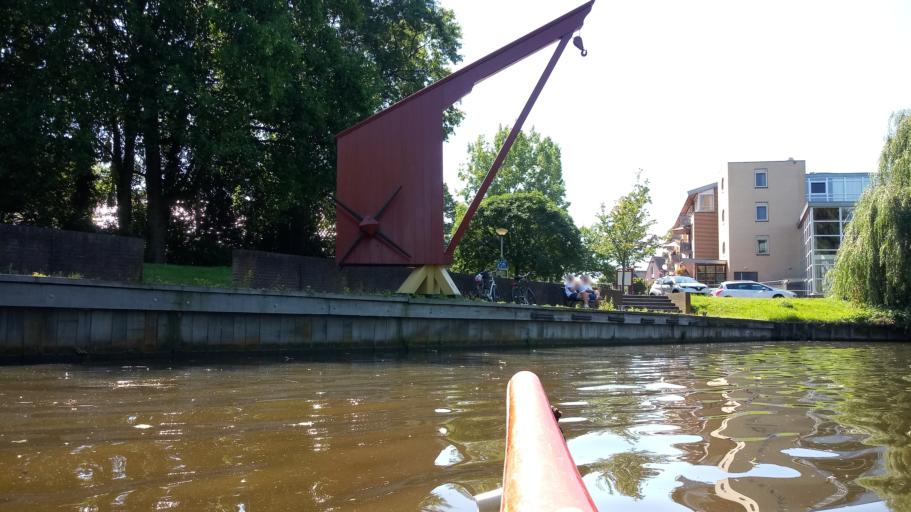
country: NL
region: Gelderland
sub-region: Berkelland
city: Eibergen
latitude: 52.1042
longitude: 6.6474
